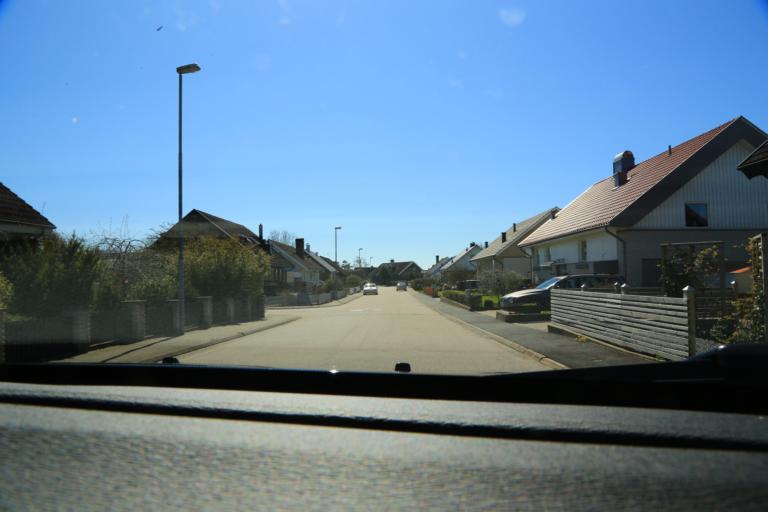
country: SE
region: Halland
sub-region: Varbergs Kommun
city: Traslovslage
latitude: 57.0524
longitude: 12.2835
